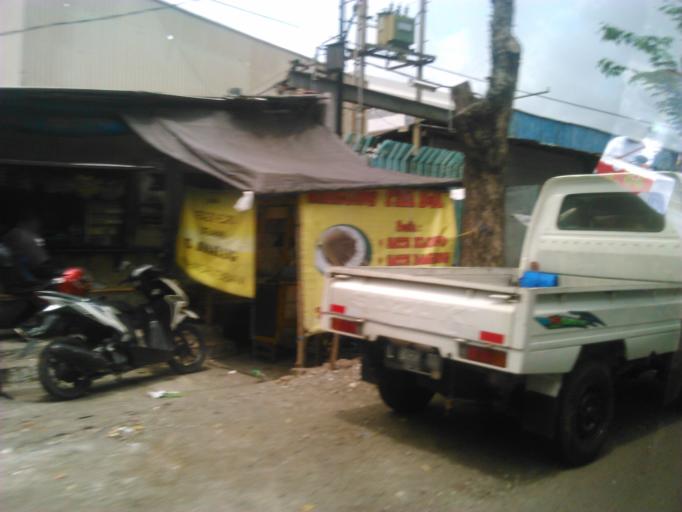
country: ID
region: East Java
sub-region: Kota Surabaya
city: Surabaya
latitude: -7.2475
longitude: 112.7332
